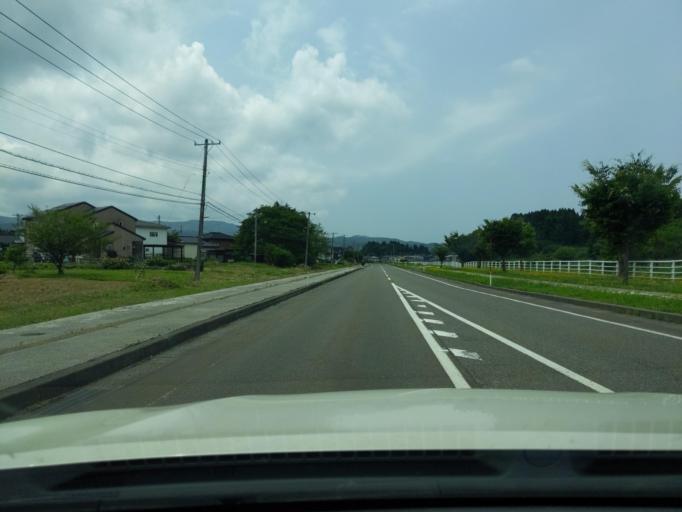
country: JP
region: Niigata
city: Kashiwazaki
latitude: 37.3323
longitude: 138.5834
